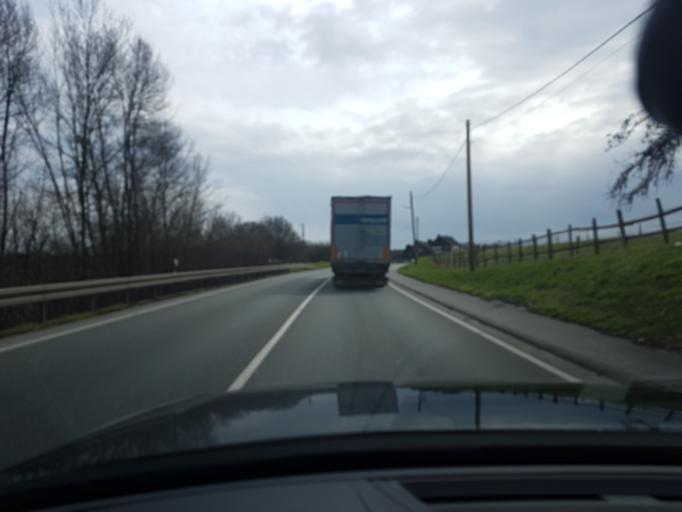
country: DE
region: North Rhine-Westphalia
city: Iserlohn
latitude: 51.4348
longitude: 7.6783
